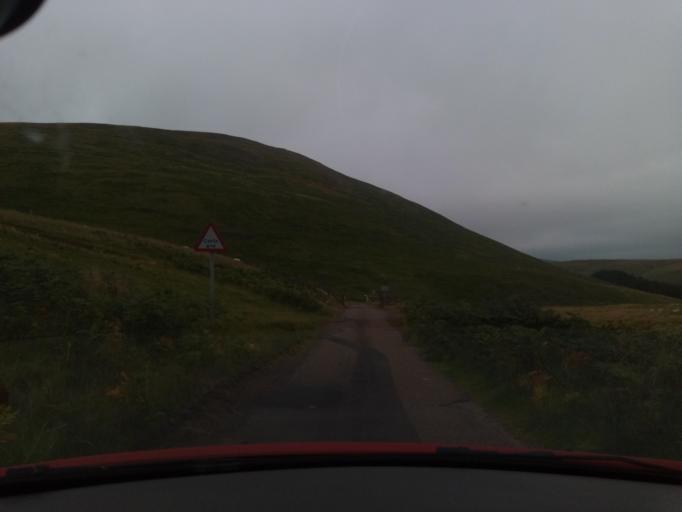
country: GB
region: England
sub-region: Northumberland
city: Rochester
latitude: 55.3967
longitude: -2.2252
